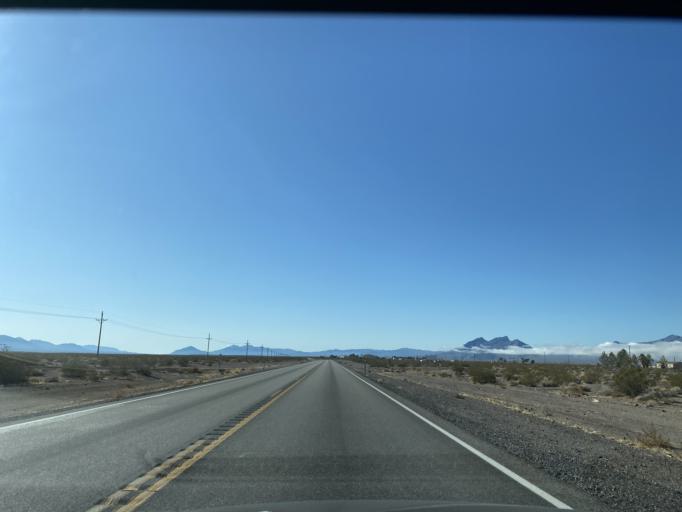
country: US
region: Nevada
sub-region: Nye County
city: Beatty
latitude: 36.5077
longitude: -116.4209
